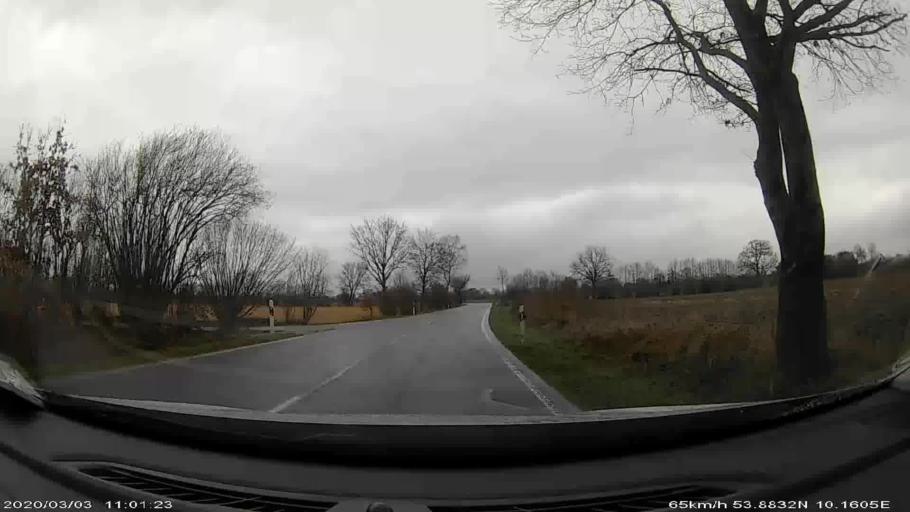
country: DE
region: Schleswig-Holstein
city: Todesfelde
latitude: 53.8857
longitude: 10.1625
